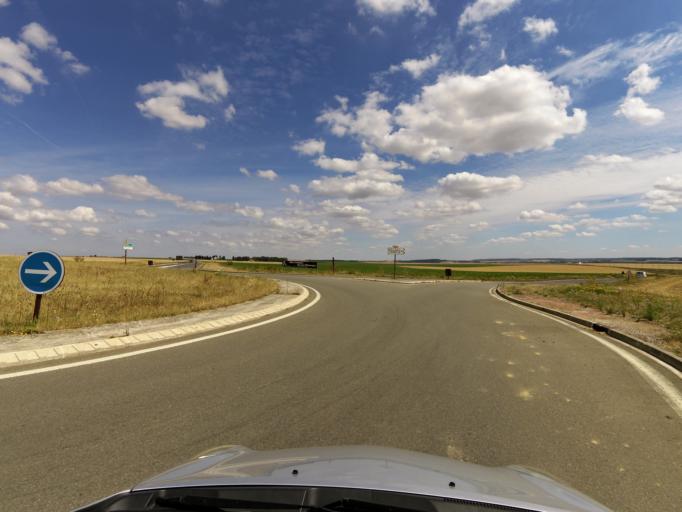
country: FR
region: Ile-de-France
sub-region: Departement de Seine-et-Marne
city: Lizy-sur-Ourcq
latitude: 49.0370
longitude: 2.9872
